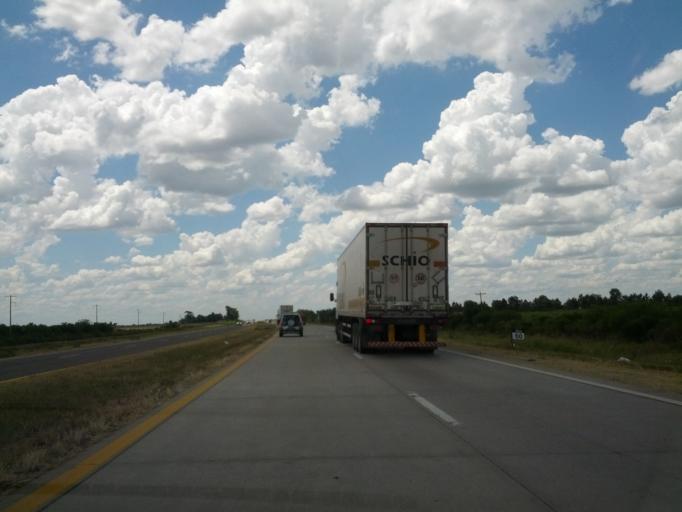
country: AR
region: Entre Rios
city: Gualeguaychu
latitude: -33.0059
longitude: -58.6043
